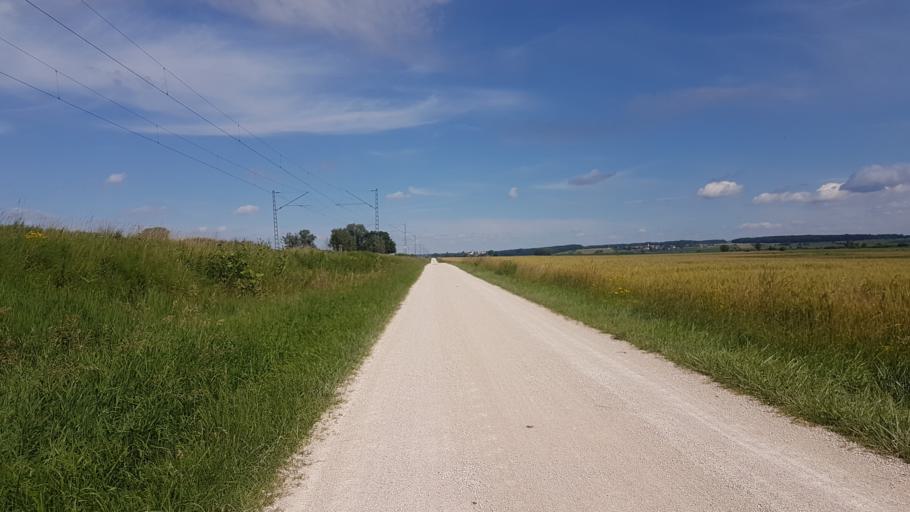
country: DE
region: Bavaria
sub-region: Regierungsbezirk Mittelfranken
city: Markt Berolzheim
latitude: 49.0224
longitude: 10.8490
